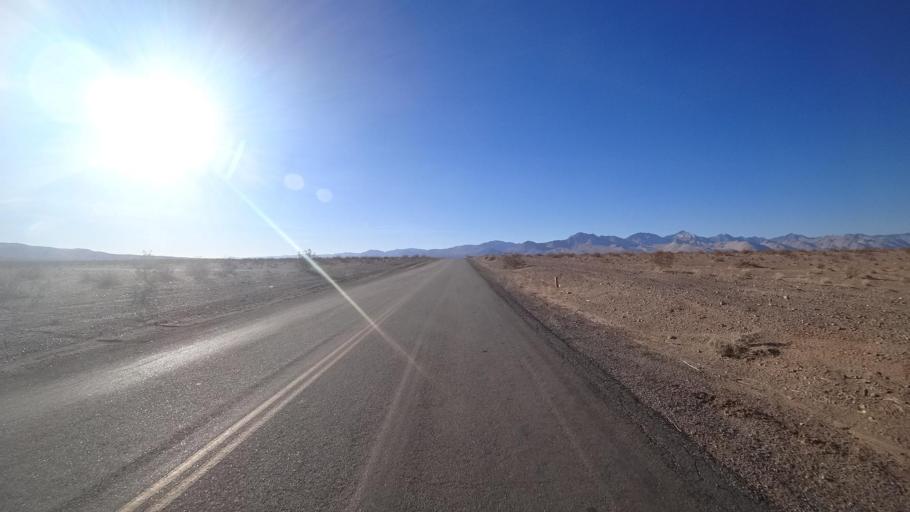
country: US
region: California
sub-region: Kern County
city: China Lake Acres
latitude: 35.6076
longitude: -117.7562
